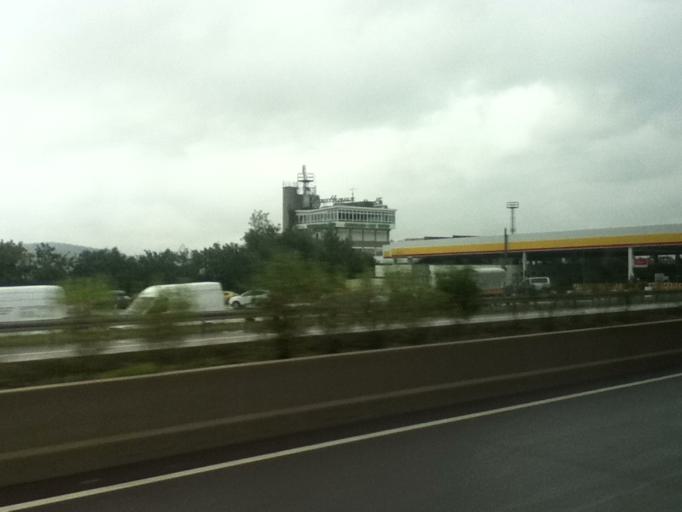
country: DE
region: Thuringia
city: Krauthausen
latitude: 51.0071
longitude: 10.2507
